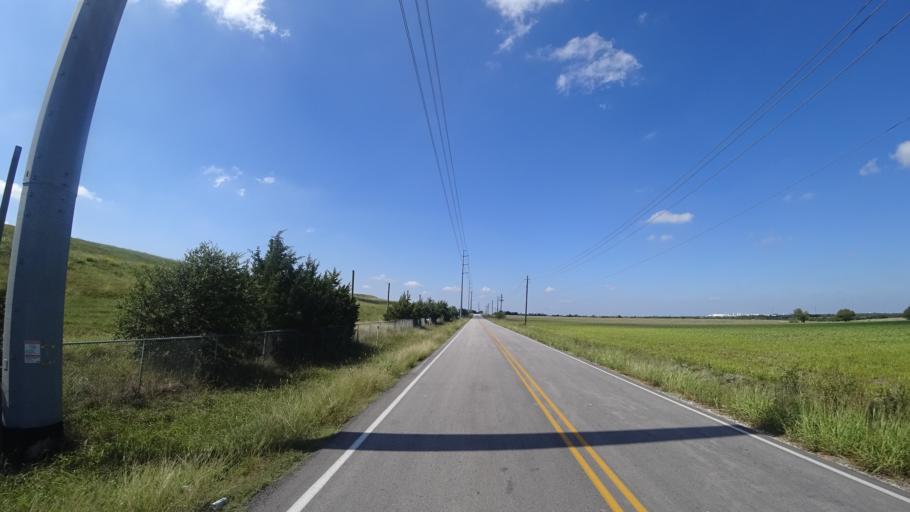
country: US
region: Texas
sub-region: Travis County
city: Manor
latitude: 30.3478
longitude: -97.6258
